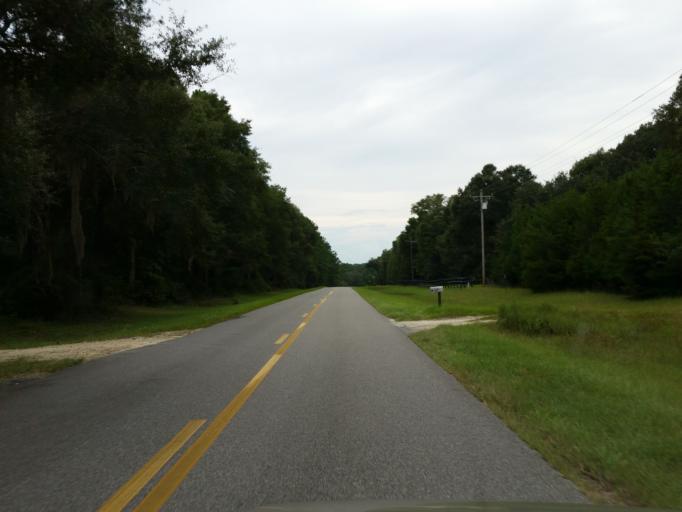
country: US
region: Florida
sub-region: Alachua County
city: High Springs
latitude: 29.9509
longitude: -82.5241
